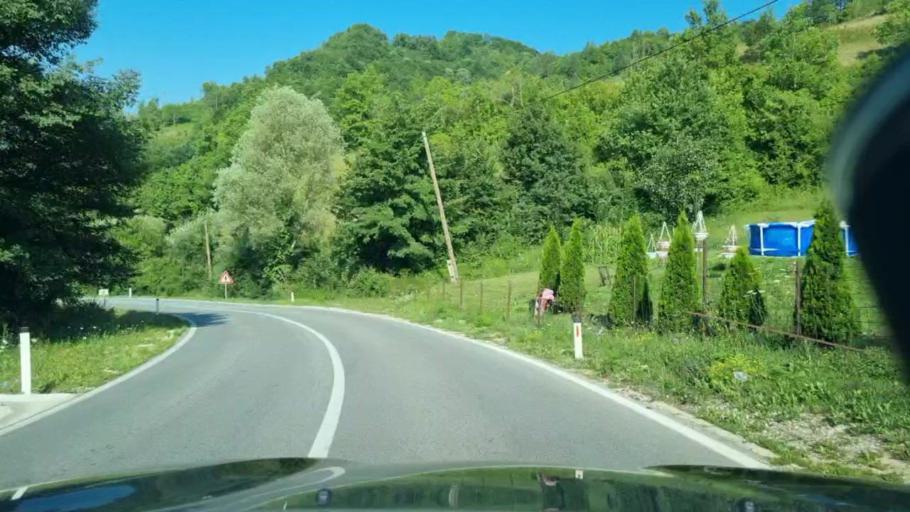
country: BA
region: Federation of Bosnia and Herzegovina
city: Jajce
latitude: 44.3479
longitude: 17.2227
